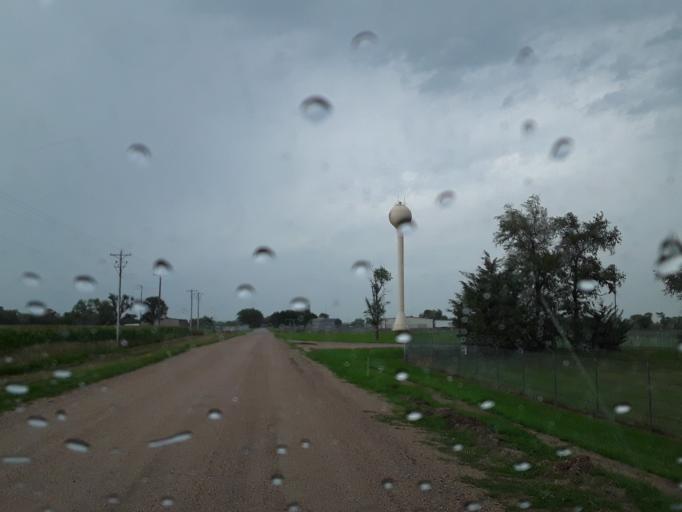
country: US
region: Nebraska
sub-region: Saunders County
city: Yutan
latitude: 41.1835
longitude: -96.4449
